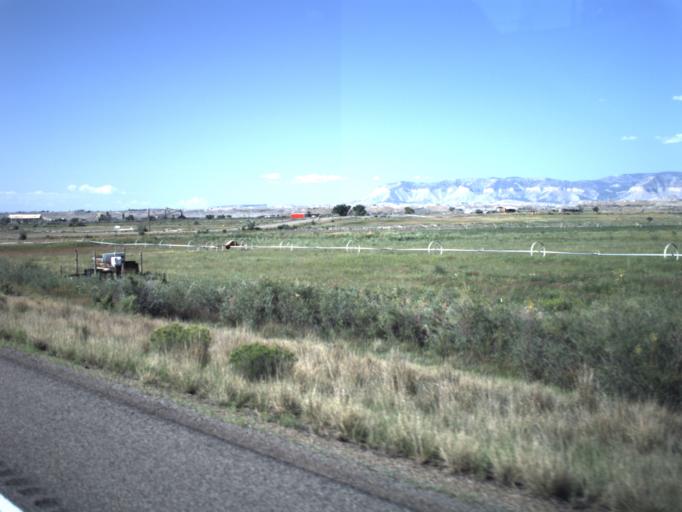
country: US
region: Utah
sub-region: Emery County
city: Castle Dale
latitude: 39.1936
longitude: -111.0243
